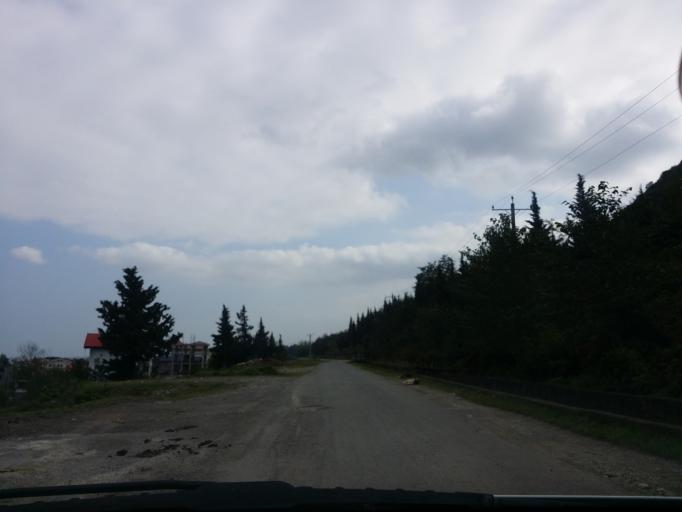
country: IR
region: Mazandaran
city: Chalus
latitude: 36.6513
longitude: 51.3548
